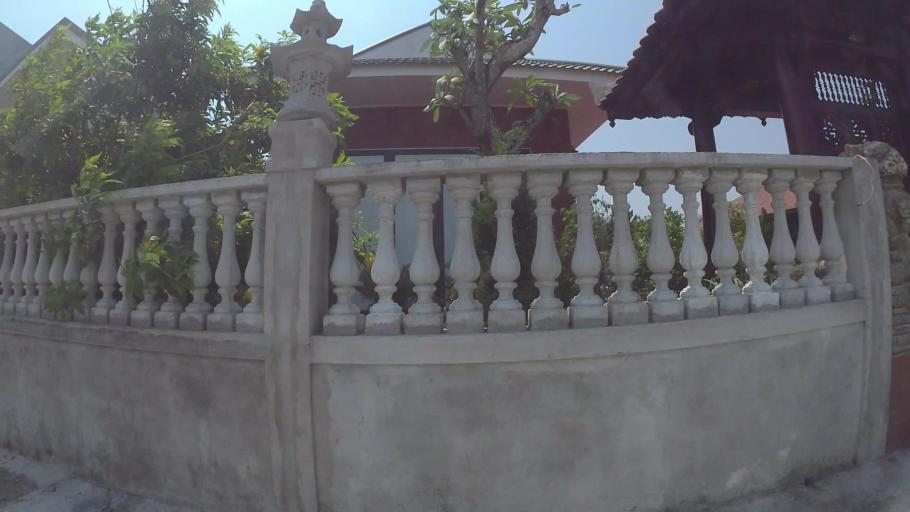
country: VN
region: Da Nang
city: Ngu Hanh Son
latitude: 15.9968
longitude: 108.2652
